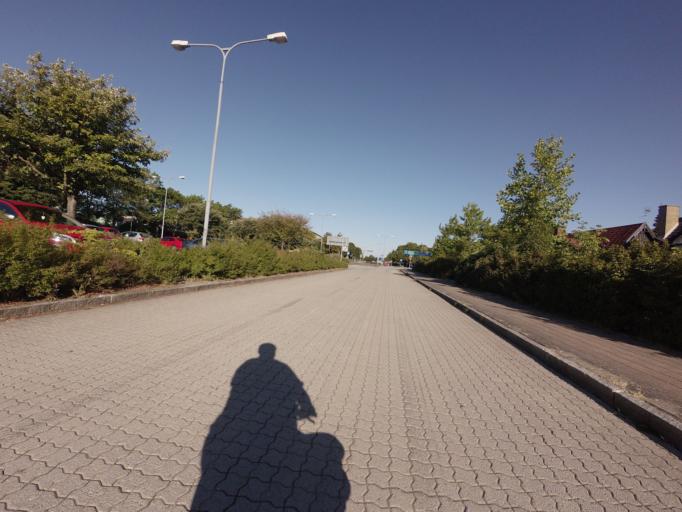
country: SE
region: Skane
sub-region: Trelleborgs Kommun
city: Trelleborg
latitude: 55.3773
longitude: 13.1571
